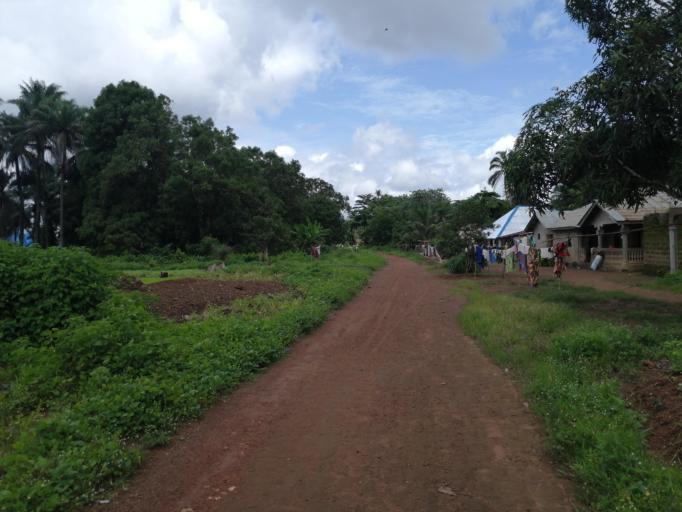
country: SL
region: Northern Province
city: Port Loko
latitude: 8.7904
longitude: -12.7718
